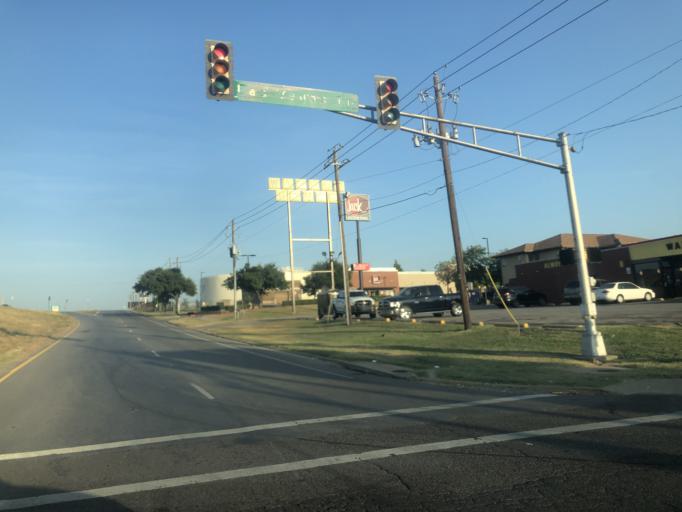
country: US
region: Texas
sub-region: Tarrant County
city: White Settlement
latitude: 32.7386
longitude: -97.4669
